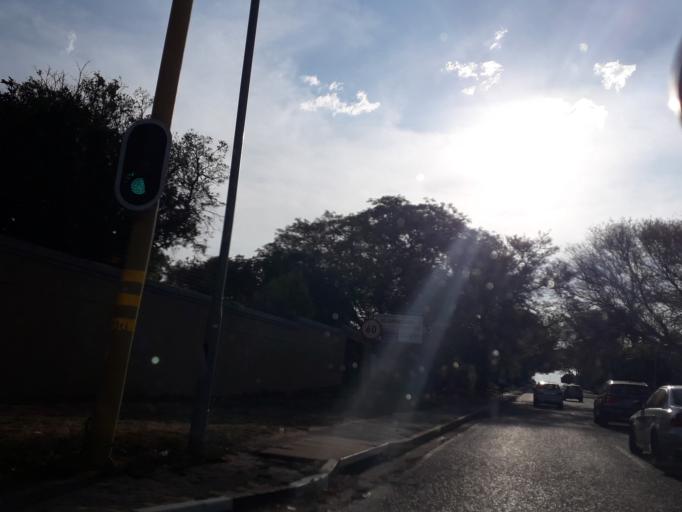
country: ZA
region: Gauteng
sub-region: City of Johannesburg Metropolitan Municipality
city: Johannesburg
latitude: -26.1164
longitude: 28.0064
